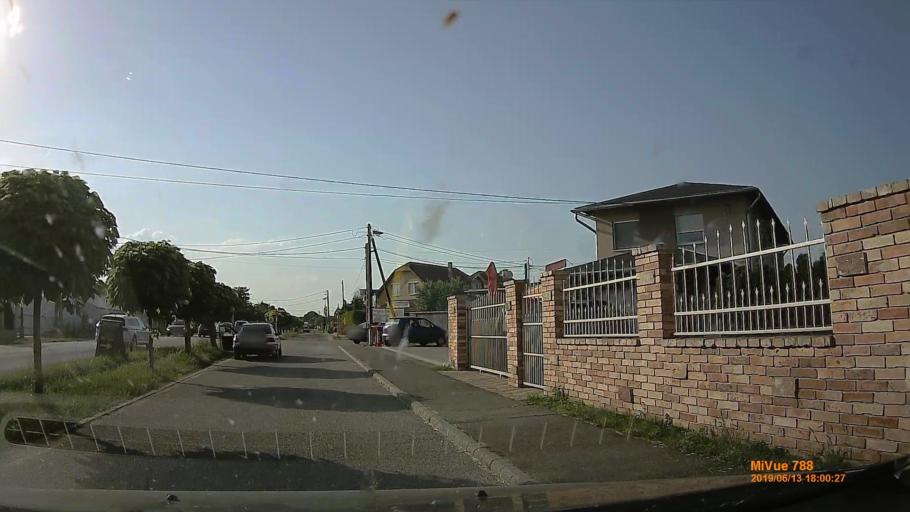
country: HU
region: Pest
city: Ecser
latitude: 47.4477
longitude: 19.3089
